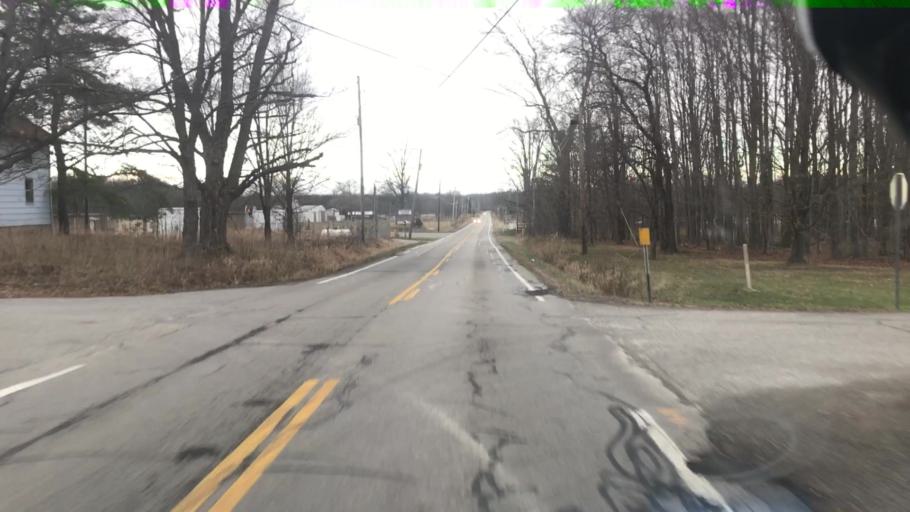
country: US
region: Ohio
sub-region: Trumbull County
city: Newton Falls
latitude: 41.2525
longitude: -80.9773
